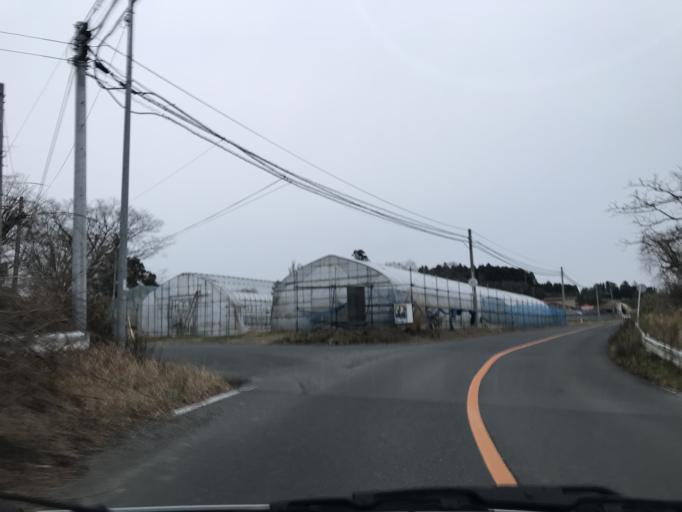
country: JP
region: Miyagi
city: Kogota
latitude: 38.7078
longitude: 141.1019
